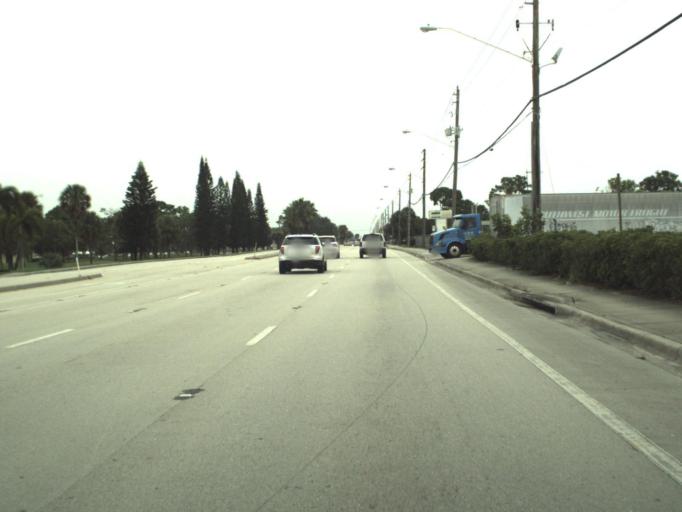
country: US
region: Florida
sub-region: Palm Beach County
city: Mangonia Park
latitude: 26.7653
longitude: -80.1079
